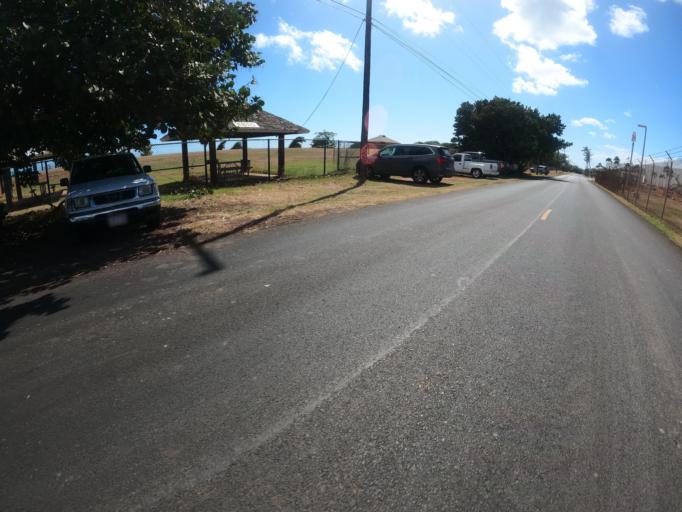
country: US
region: Hawaii
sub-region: Honolulu County
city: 'Ewa Villages
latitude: 21.3006
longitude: -158.0686
